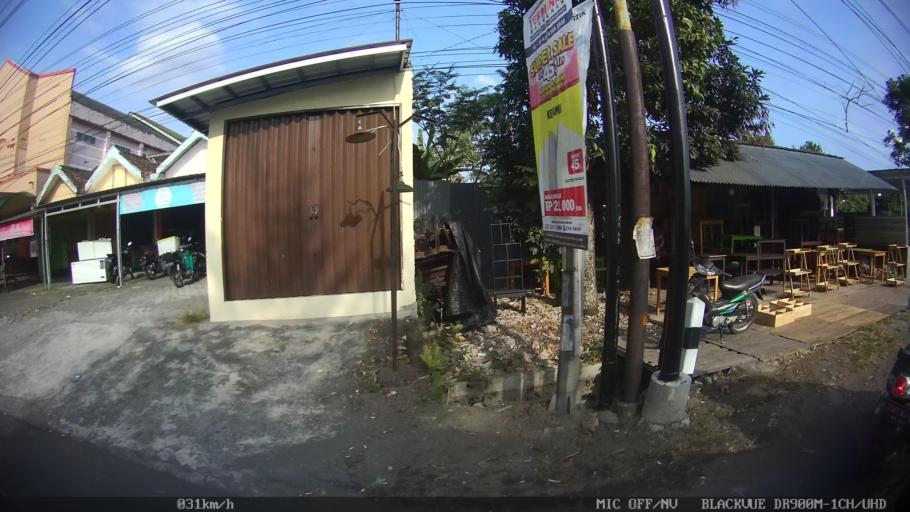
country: ID
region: Daerah Istimewa Yogyakarta
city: Melati
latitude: -7.7130
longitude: 110.4079
